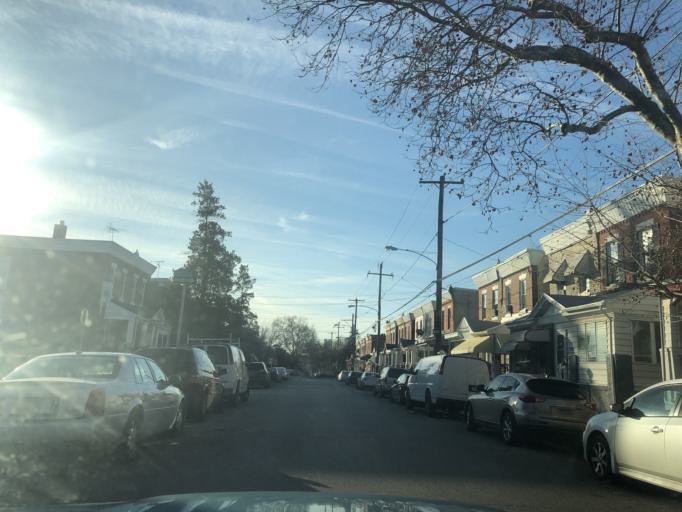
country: US
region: Pennsylvania
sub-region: Delaware County
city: Millbourne
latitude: 39.9736
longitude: -75.2292
